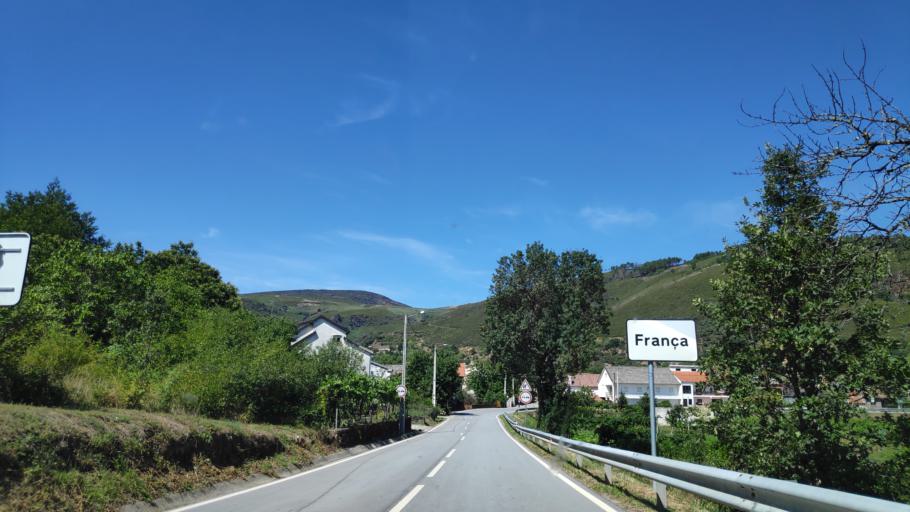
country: PT
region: Braganca
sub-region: Braganca Municipality
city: Braganca
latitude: 41.9005
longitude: -6.7338
